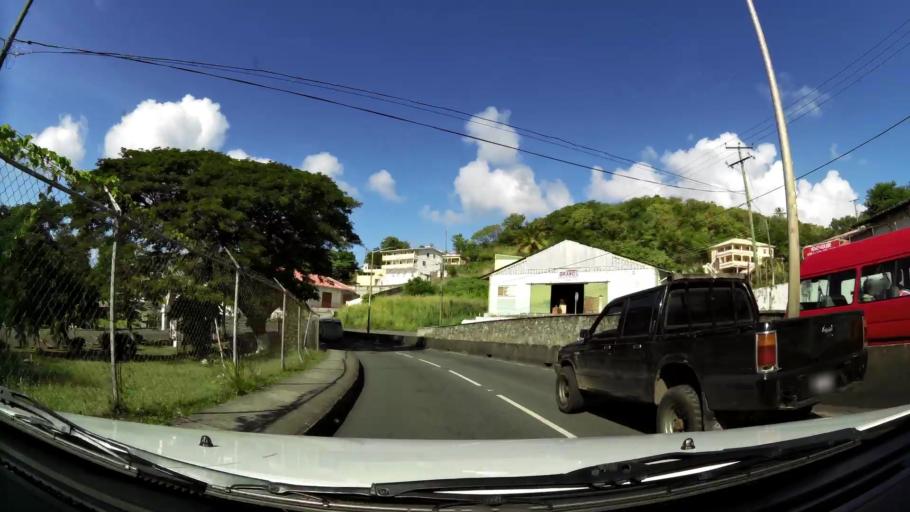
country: LC
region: Castries Quarter
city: Bisee
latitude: 14.0267
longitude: -60.9777
